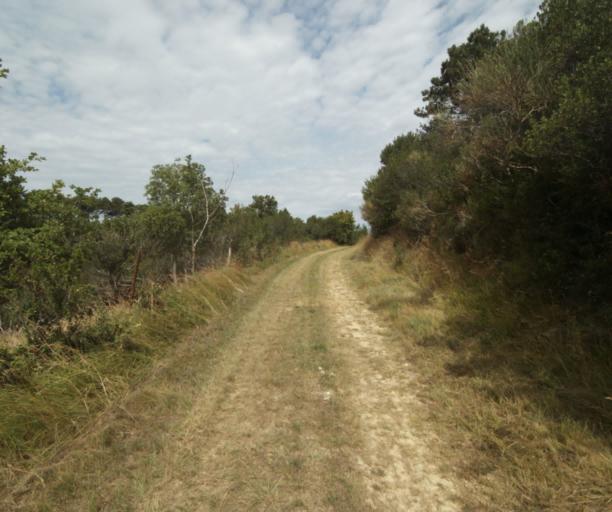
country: FR
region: Midi-Pyrenees
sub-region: Departement de la Haute-Garonne
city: Saint-Felix-Lauragais
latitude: 43.4457
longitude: 1.9011
